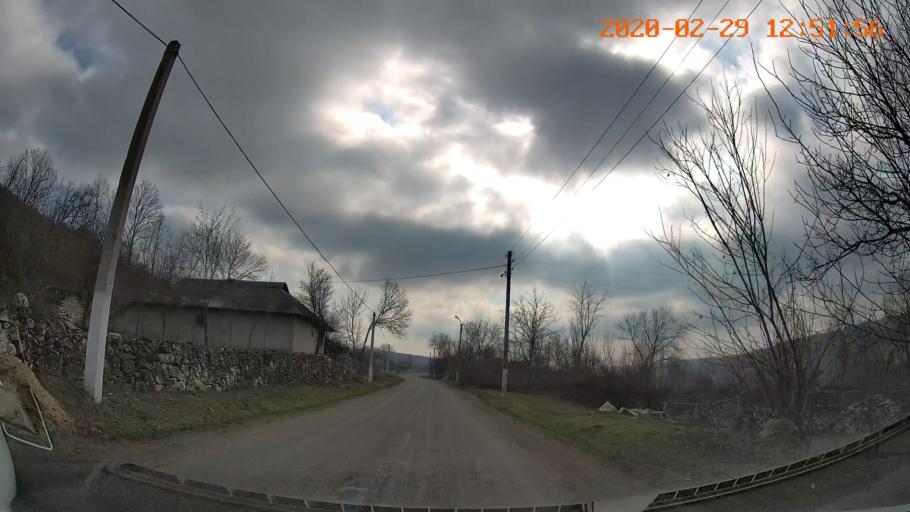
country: MD
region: Telenesti
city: Camenca
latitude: 48.1158
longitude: 28.7318
